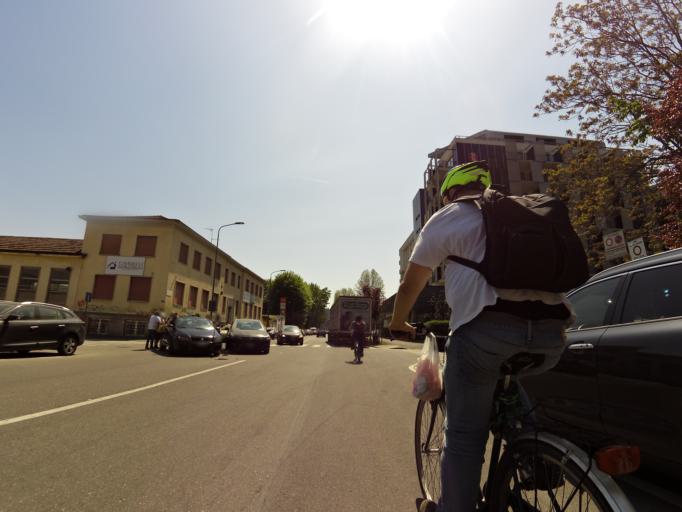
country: IT
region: Lombardy
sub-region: Citta metropolitana di Milano
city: Sesto San Giovanni
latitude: 45.5023
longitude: 9.2281
